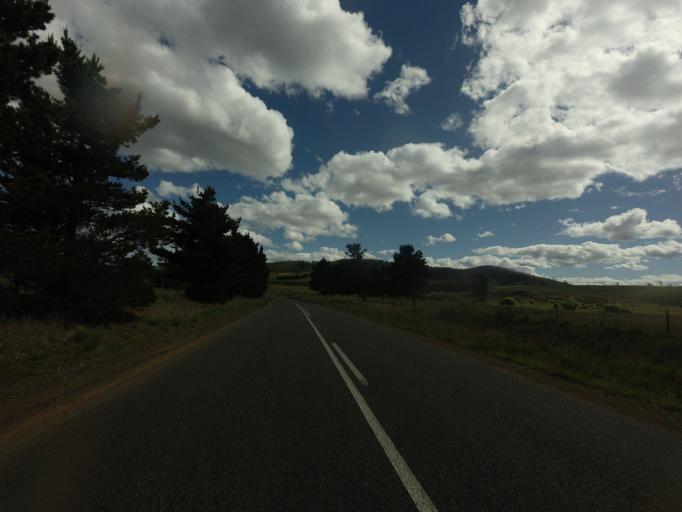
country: AU
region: Tasmania
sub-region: Brighton
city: Bridgewater
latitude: -42.4010
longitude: 147.3115
